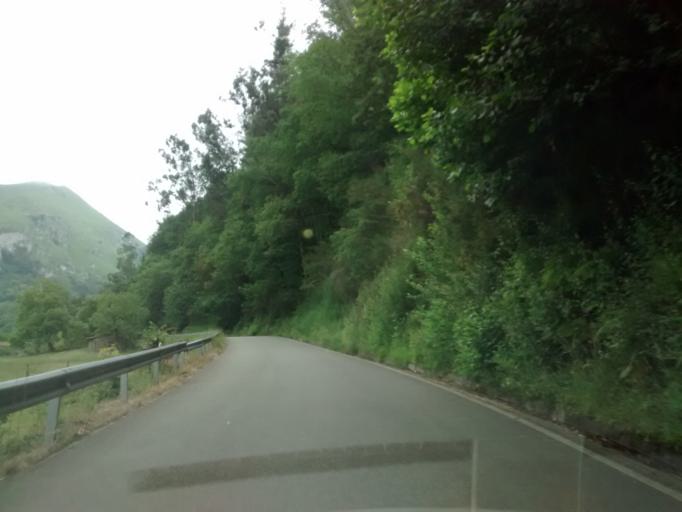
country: ES
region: Asturias
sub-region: Province of Asturias
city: Pilona
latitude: 43.3048
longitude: -5.3637
